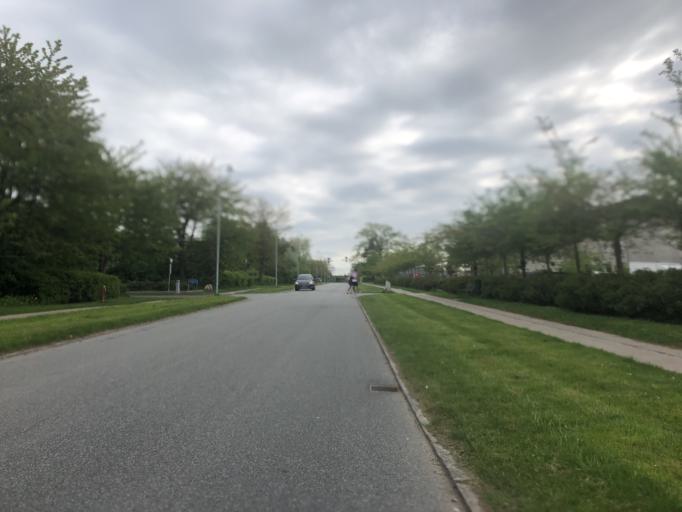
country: DK
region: Zealand
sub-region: Koge Kommune
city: Koge
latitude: 55.4467
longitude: 12.1631
